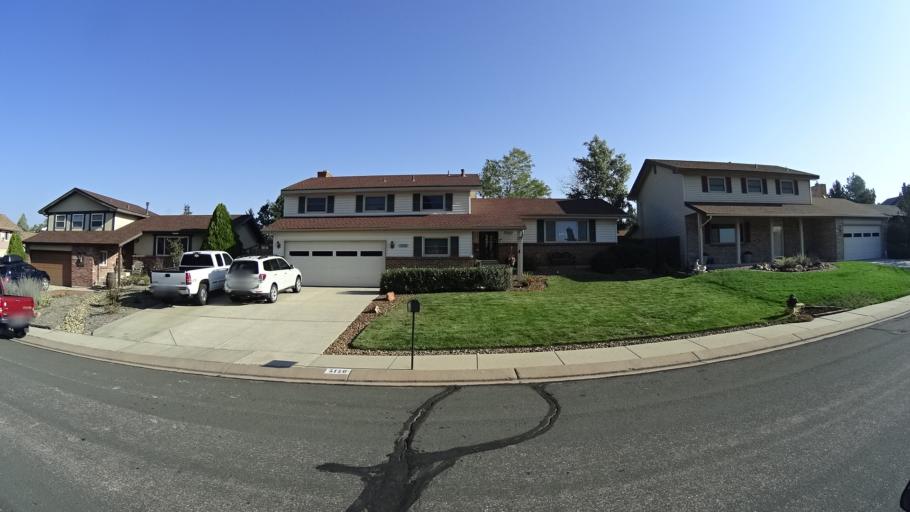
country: US
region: Colorado
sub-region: El Paso County
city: Cimarron Hills
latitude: 38.8864
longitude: -104.7323
